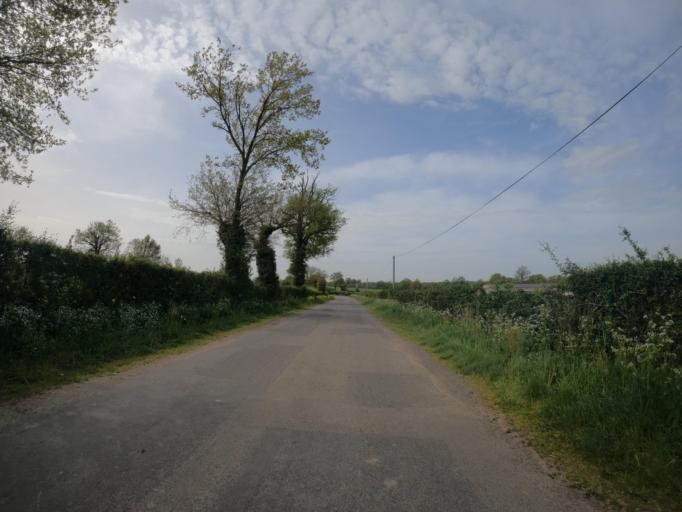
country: FR
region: Poitou-Charentes
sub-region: Departement des Deux-Sevres
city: Moncoutant
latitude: 46.6970
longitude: -0.5514
